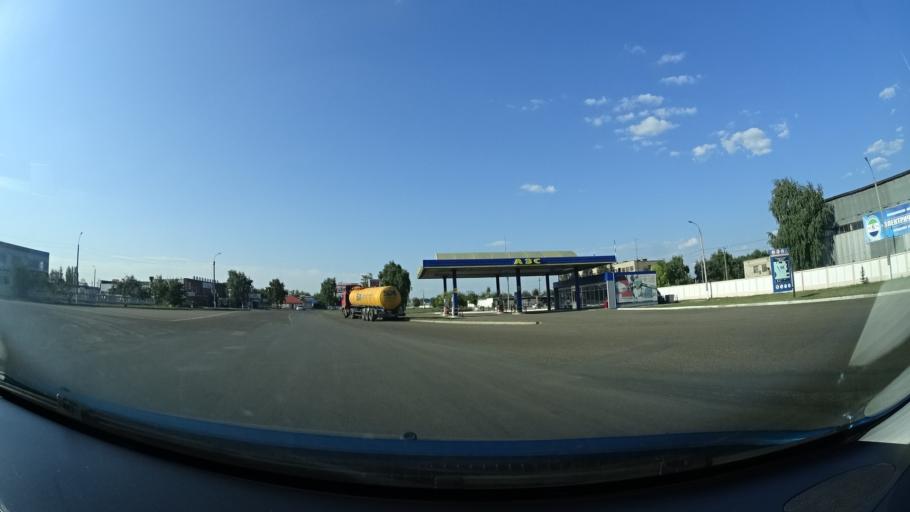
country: RU
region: Bashkortostan
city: Salavat
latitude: 53.3736
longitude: 55.9256
